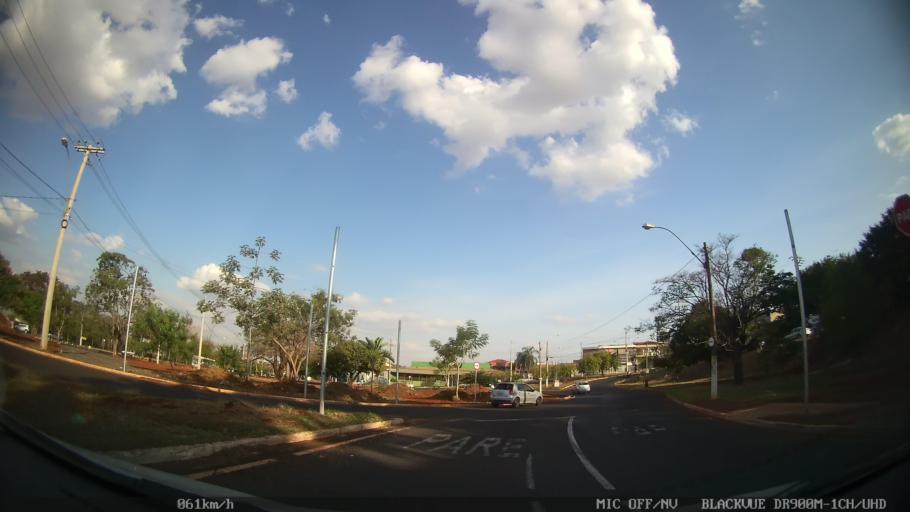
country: BR
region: Sao Paulo
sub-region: Ribeirao Preto
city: Ribeirao Preto
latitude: -21.1388
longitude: -47.8348
